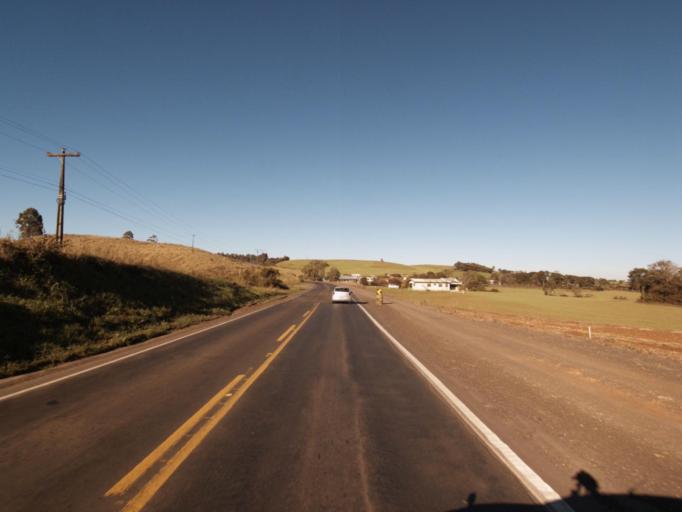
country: AR
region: Misiones
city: Bernardo de Irigoyen
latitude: -26.6128
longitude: -53.5187
